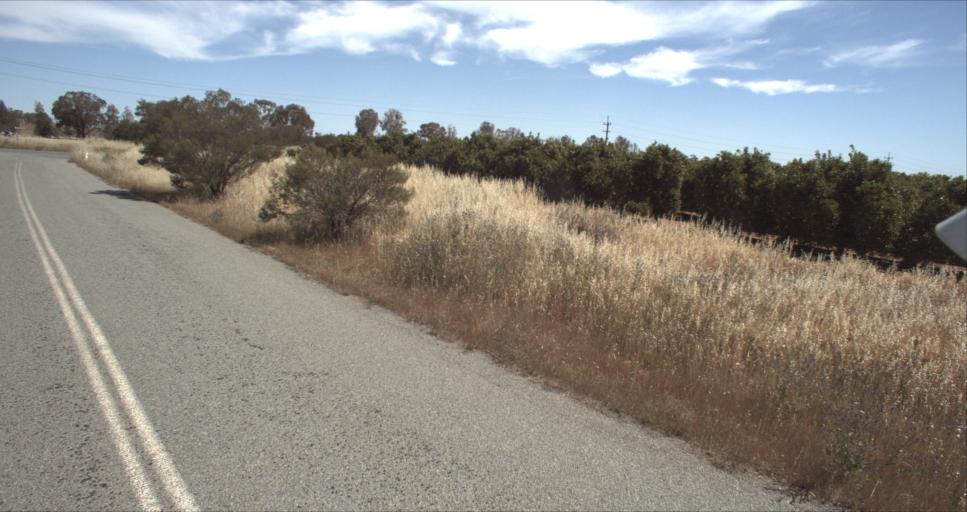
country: AU
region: New South Wales
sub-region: Leeton
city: Leeton
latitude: -34.6144
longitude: 146.4339
